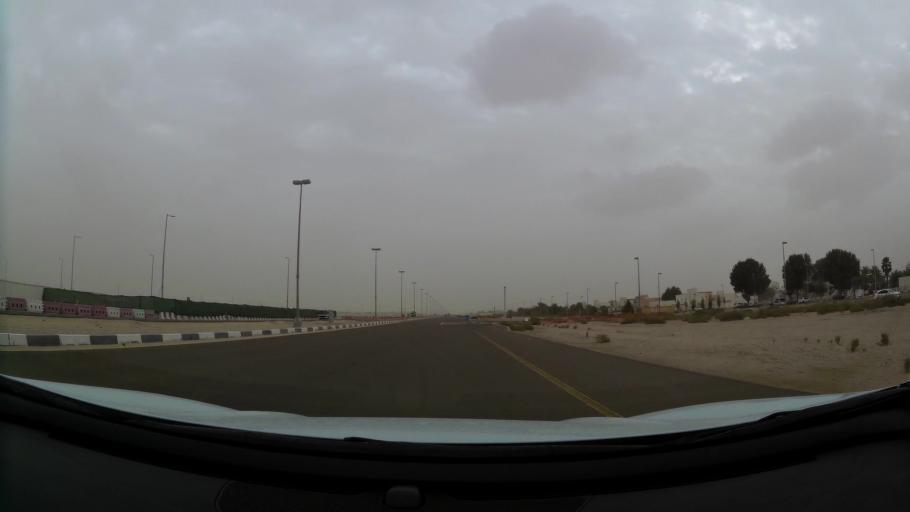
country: AE
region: Abu Dhabi
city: Abu Dhabi
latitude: 24.4265
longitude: 54.7200
